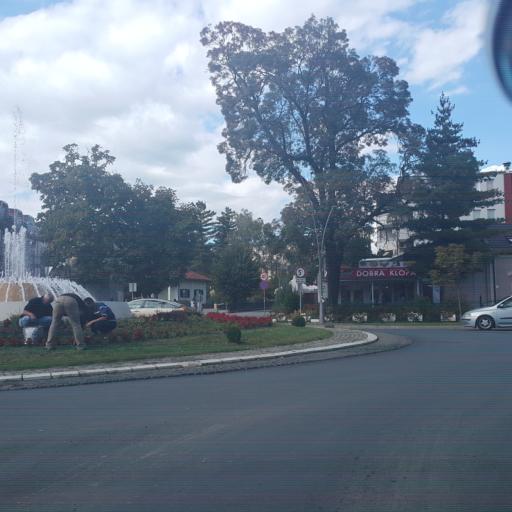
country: RS
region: Central Serbia
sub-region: Raski Okrug
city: Vrnjacka Banja
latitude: 43.6251
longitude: 20.8954
